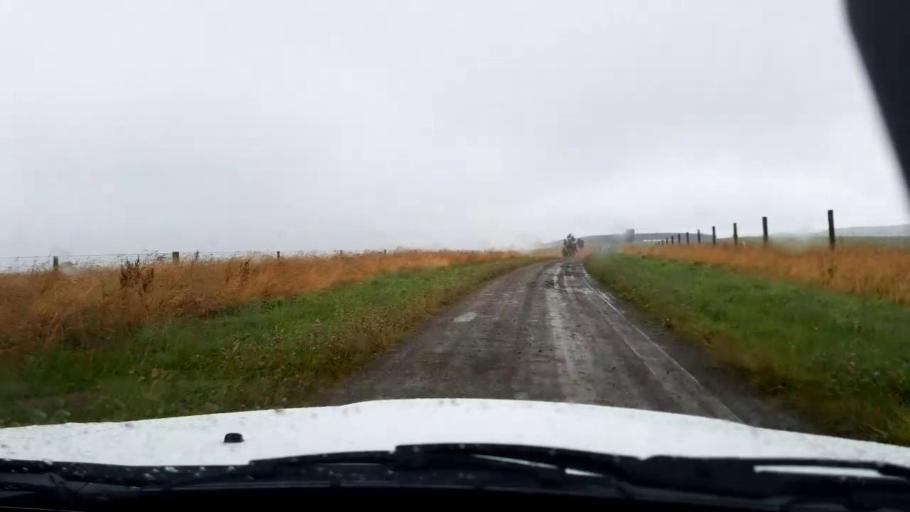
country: NZ
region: Canterbury
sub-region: Timaru District
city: Pleasant Point
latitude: -44.1691
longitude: 171.1613
